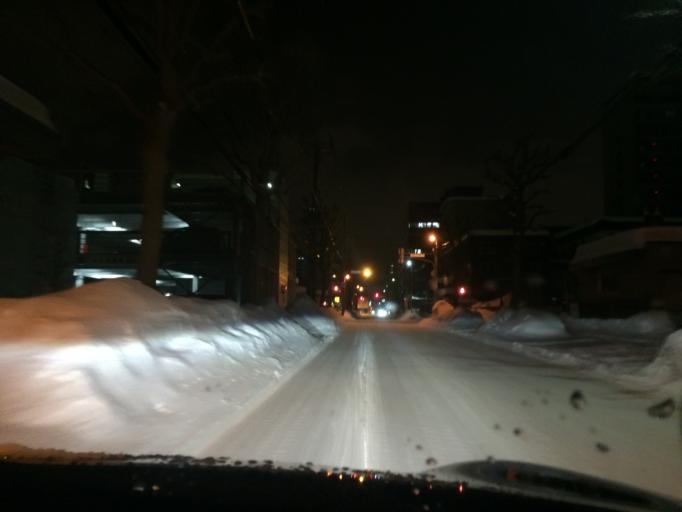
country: JP
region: Hokkaido
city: Sapporo
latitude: 43.0731
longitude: 141.3591
